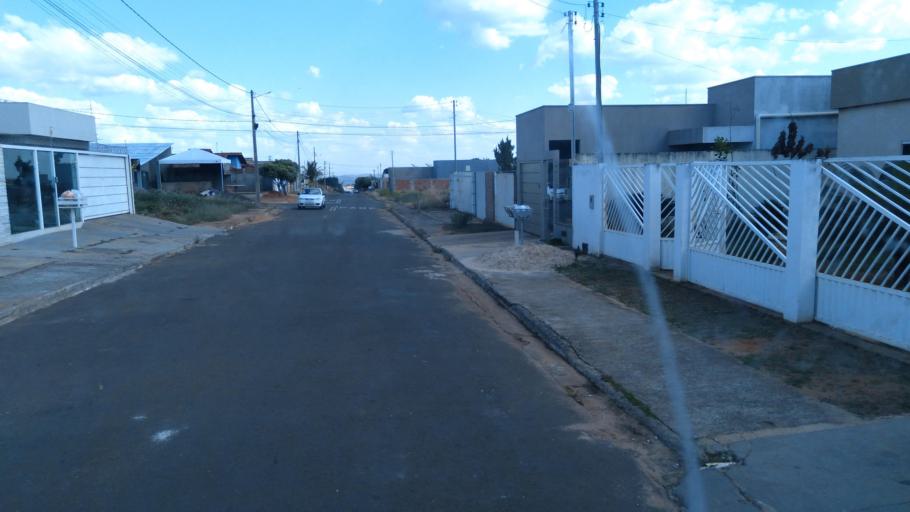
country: YE
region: Al Mahrah
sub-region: Shahan
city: Shihan as Sufla
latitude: 17.5430
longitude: 52.5394
